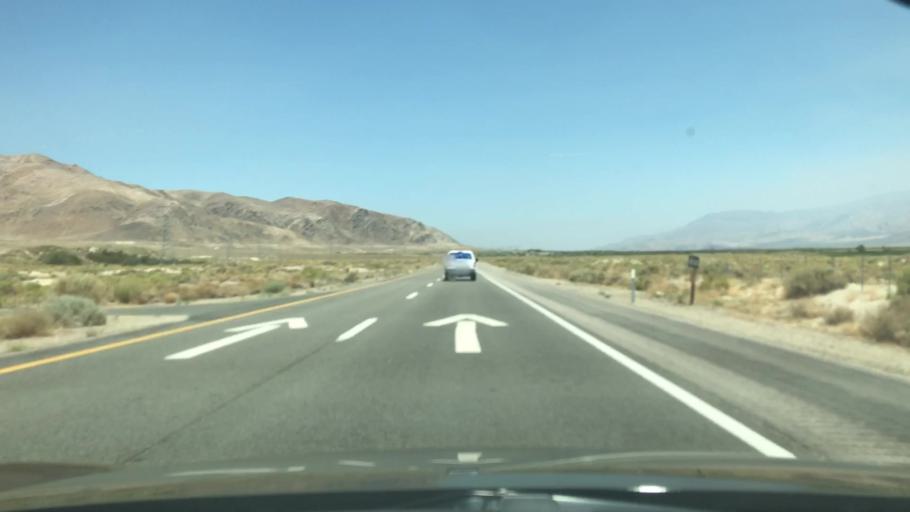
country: US
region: California
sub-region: Inyo County
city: Lone Pine
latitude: 36.6436
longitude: -118.0827
